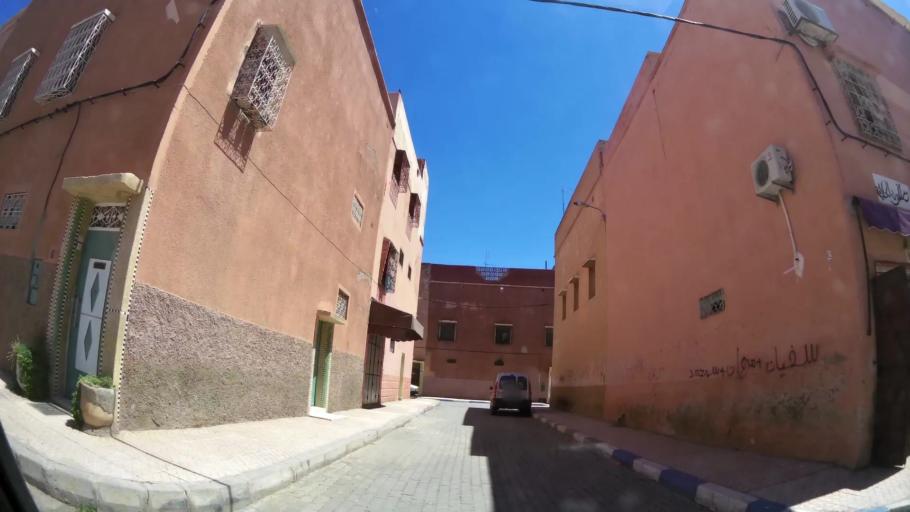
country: MA
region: Marrakech-Tensift-Al Haouz
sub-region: Marrakech
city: Marrakesh
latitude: 31.6490
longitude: -7.9922
